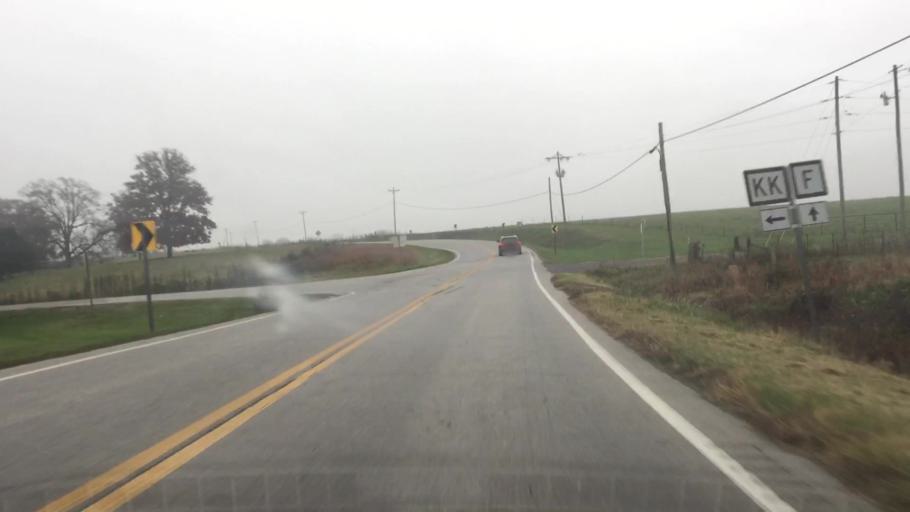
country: US
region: Missouri
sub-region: Callaway County
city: Fulton
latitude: 38.8643
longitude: -92.0123
